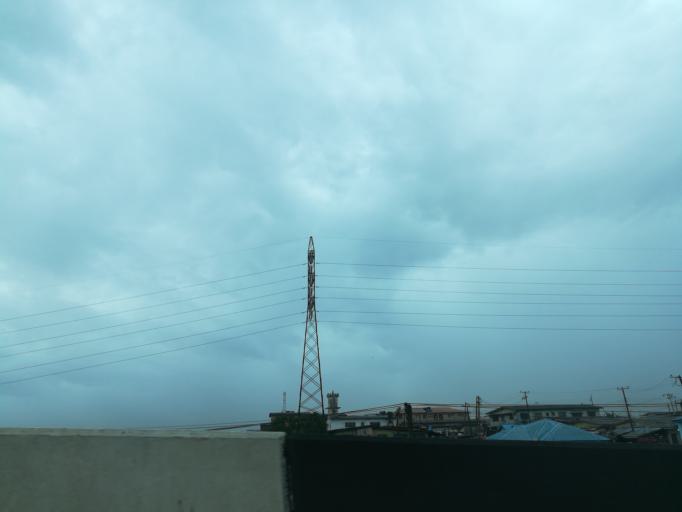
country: NG
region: Lagos
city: Ojota
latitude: 6.6065
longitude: 3.3986
